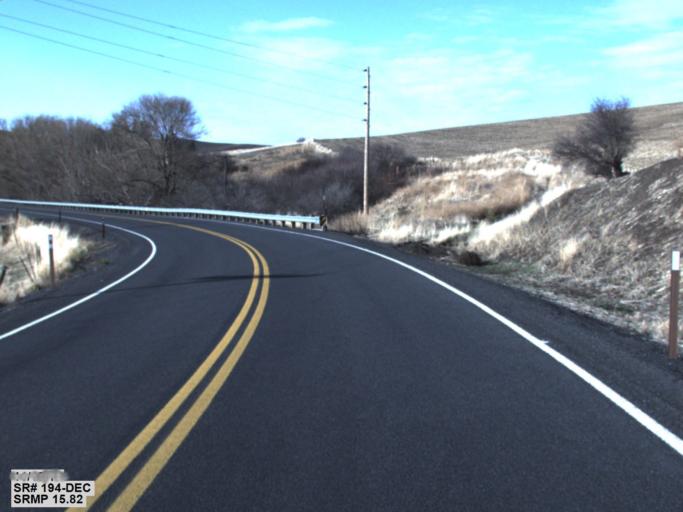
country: US
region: Washington
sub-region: Whitman County
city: Pullman
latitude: 46.7307
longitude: -117.3057
